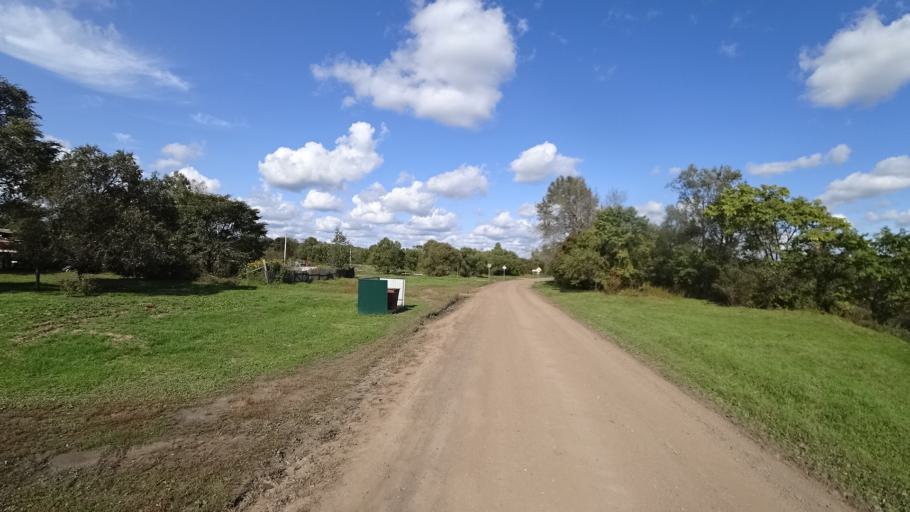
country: RU
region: Amur
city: Arkhara
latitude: 49.4055
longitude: 130.1567
